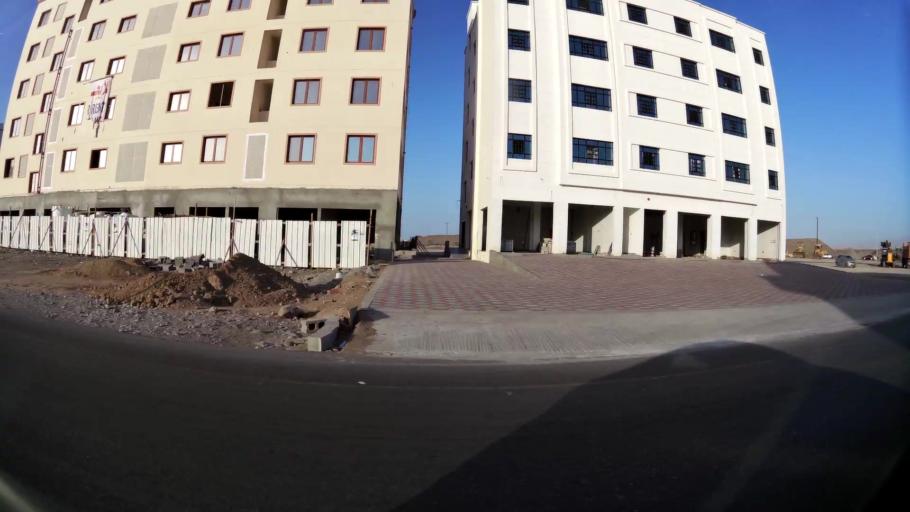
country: OM
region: Muhafazat Masqat
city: As Sib al Jadidah
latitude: 23.5865
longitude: 58.1455
